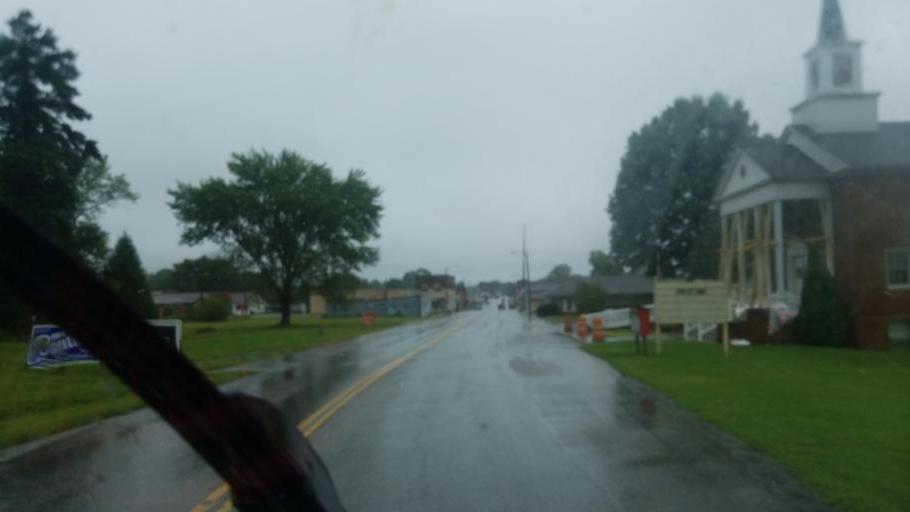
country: US
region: Kentucky
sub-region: Greenup County
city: South Shore
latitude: 38.7175
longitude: -82.9613
